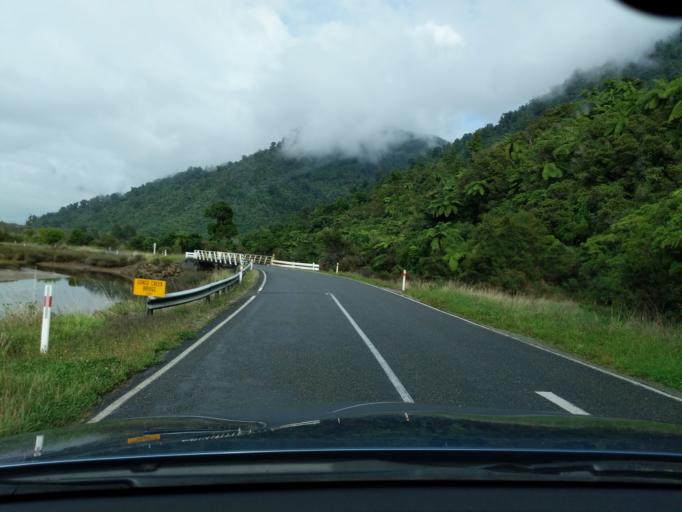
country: NZ
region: Tasman
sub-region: Tasman District
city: Takaka
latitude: -40.6556
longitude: 172.6469
